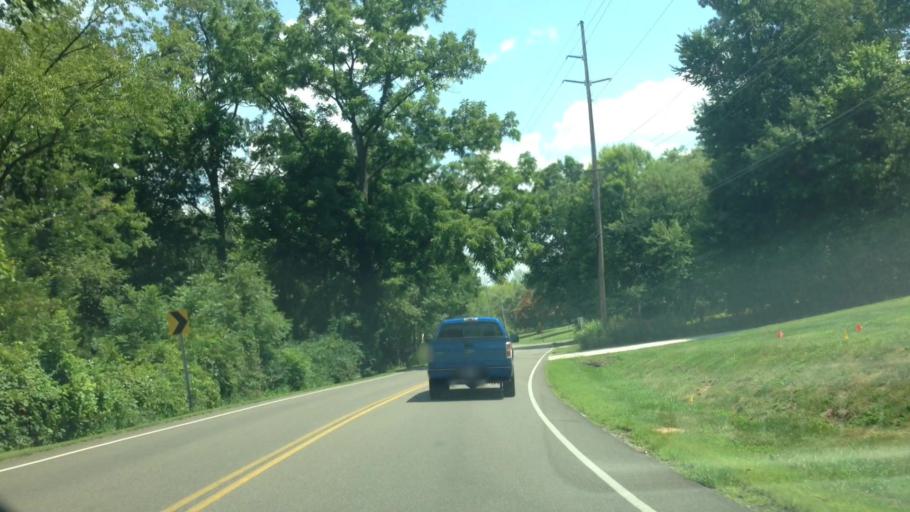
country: US
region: Ohio
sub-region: Summit County
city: New Franklin
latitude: 40.9504
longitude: -81.5487
